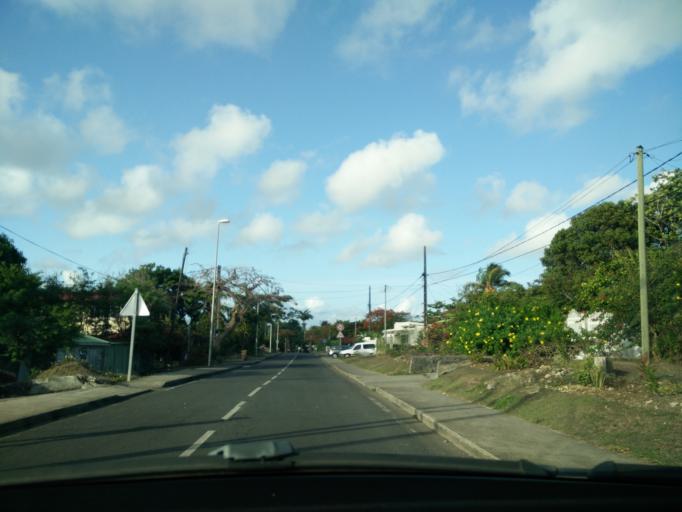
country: GP
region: Guadeloupe
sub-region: Guadeloupe
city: Le Moule
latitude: 16.3268
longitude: -61.3437
